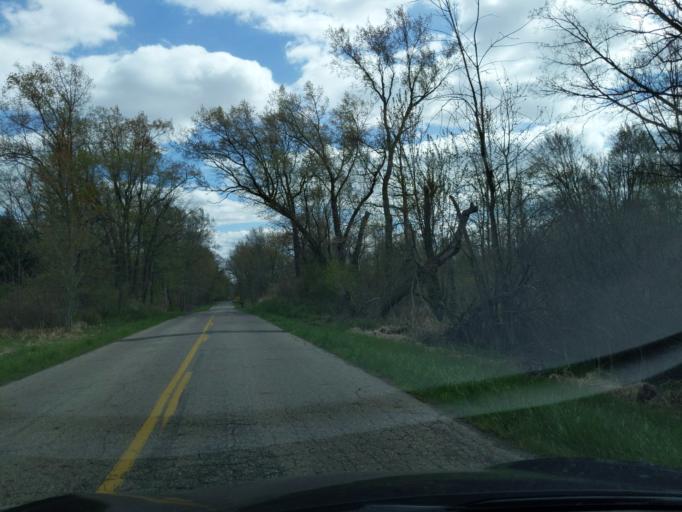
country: US
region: Michigan
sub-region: Eaton County
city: Eaton Rapids
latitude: 42.4906
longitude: -84.5463
